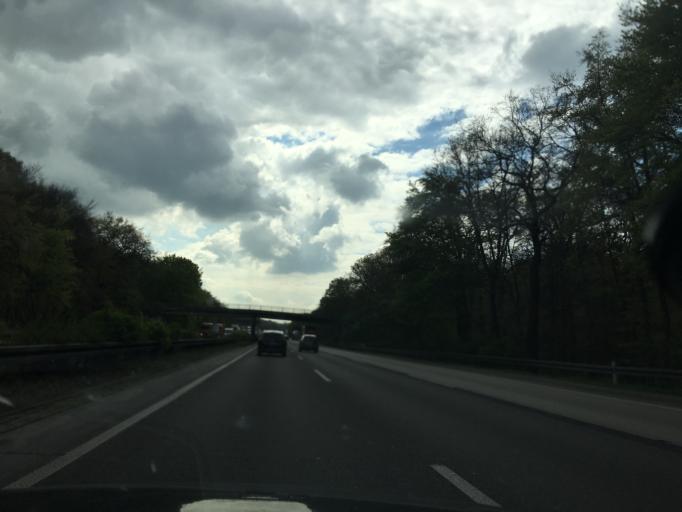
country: DE
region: North Rhine-Westphalia
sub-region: Regierungsbezirk Dusseldorf
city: Duisburg
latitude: 51.4035
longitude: 6.8062
